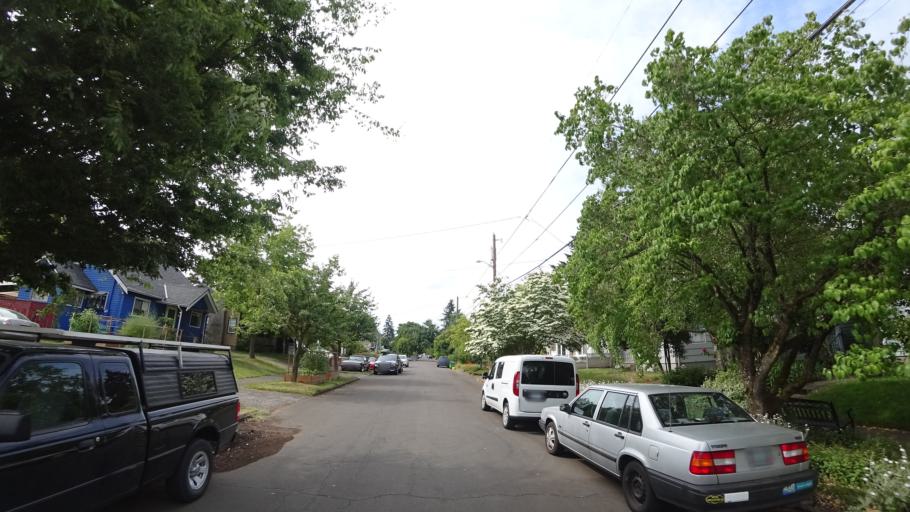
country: US
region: Oregon
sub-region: Multnomah County
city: Portland
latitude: 45.5733
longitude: -122.6853
